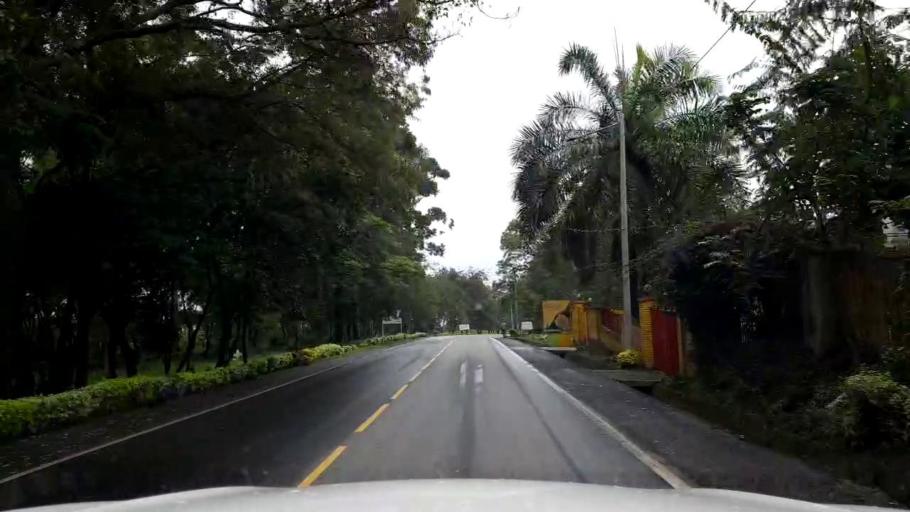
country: RW
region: Western Province
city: Gisenyi
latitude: -1.7044
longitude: 29.2676
